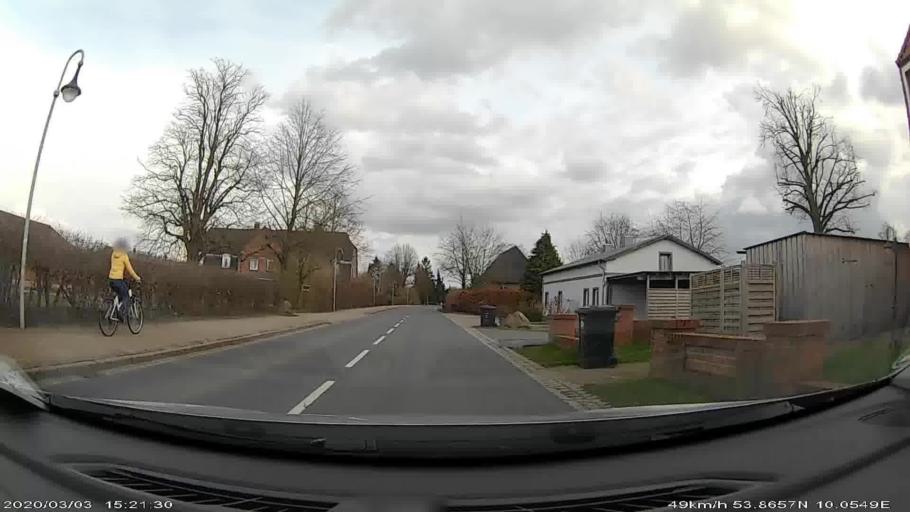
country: DE
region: Schleswig-Holstein
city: Struvenhutten
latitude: 53.8660
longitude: 10.0541
